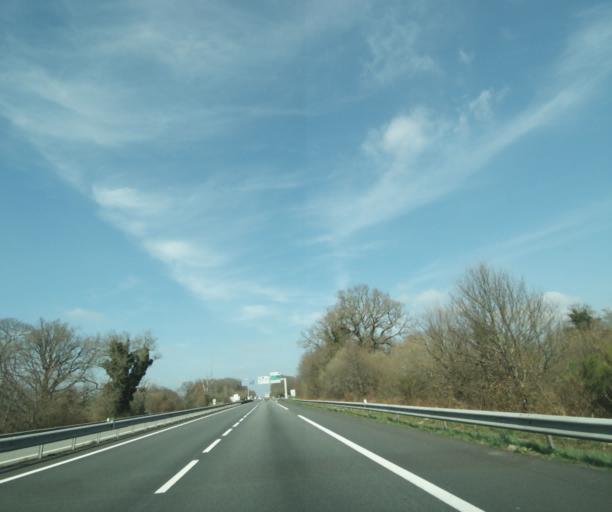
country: FR
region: Limousin
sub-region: Departement de la Creuse
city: Saint-Maurice-la-Souterraine
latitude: 46.1935
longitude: 1.3827
